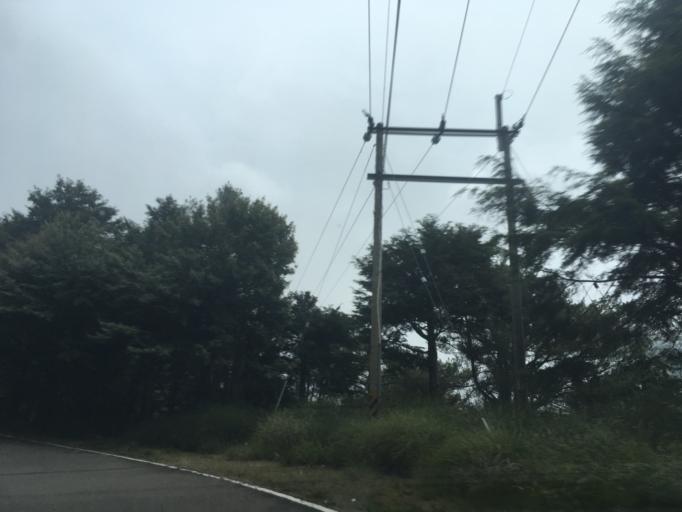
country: TW
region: Taiwan
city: Fengyuan
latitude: 24.2755
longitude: 121.0294
